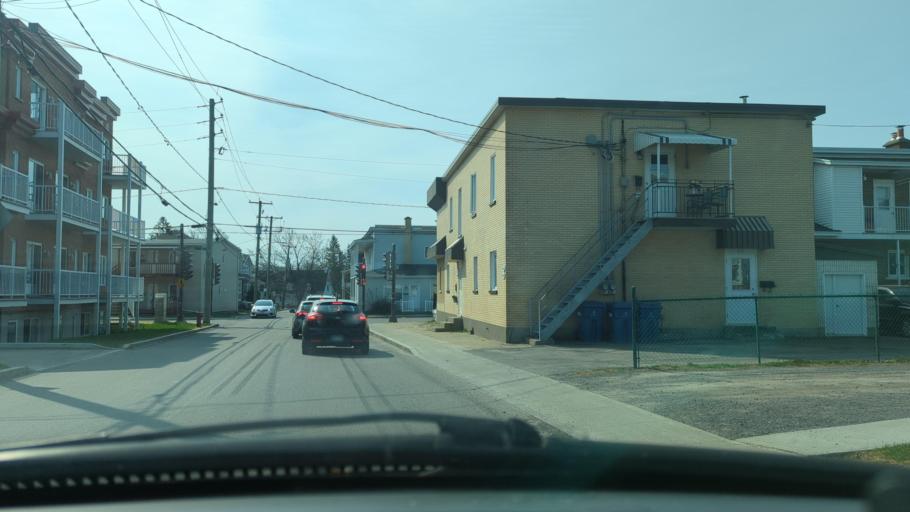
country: CA
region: Quebec
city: Quebec
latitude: 46.8521
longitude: -71.2119
